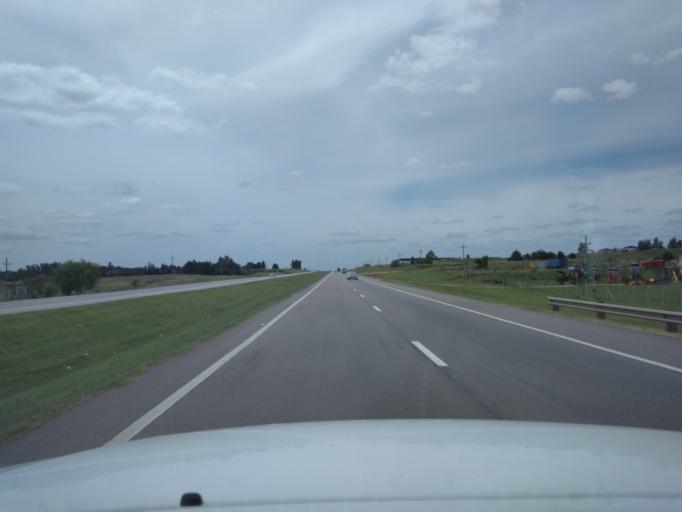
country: UY
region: Canelones
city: Las Piedras
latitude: -34.7107
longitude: -56.2425
